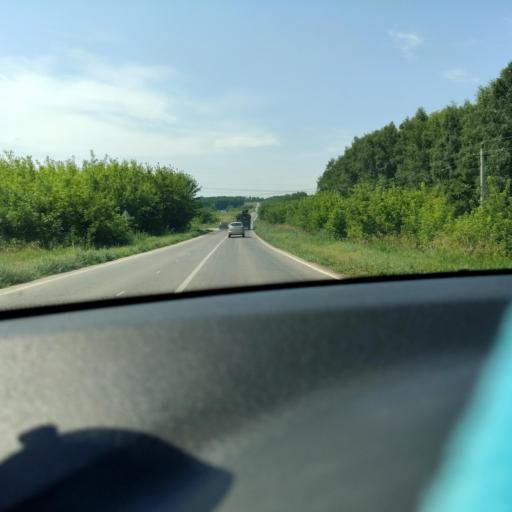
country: RU
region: Samara
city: Petra-Dubrava
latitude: 53.3454
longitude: 50.5131
